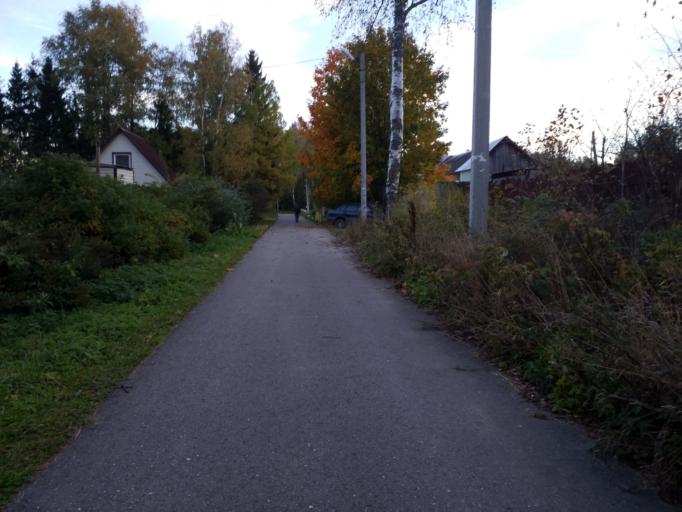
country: RU
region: Moskovskaya
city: Ashukino
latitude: 56.1681
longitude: 37.9547
